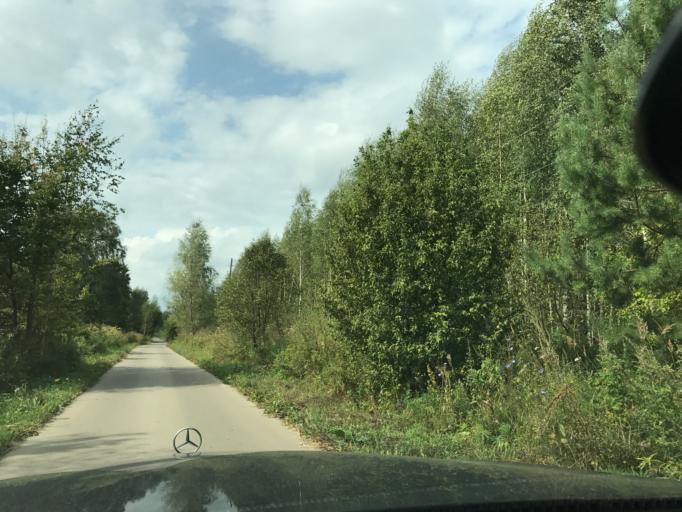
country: RU
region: Nizjnij Novgorod
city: Vacha
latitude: 55.9767
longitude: 42.7624
